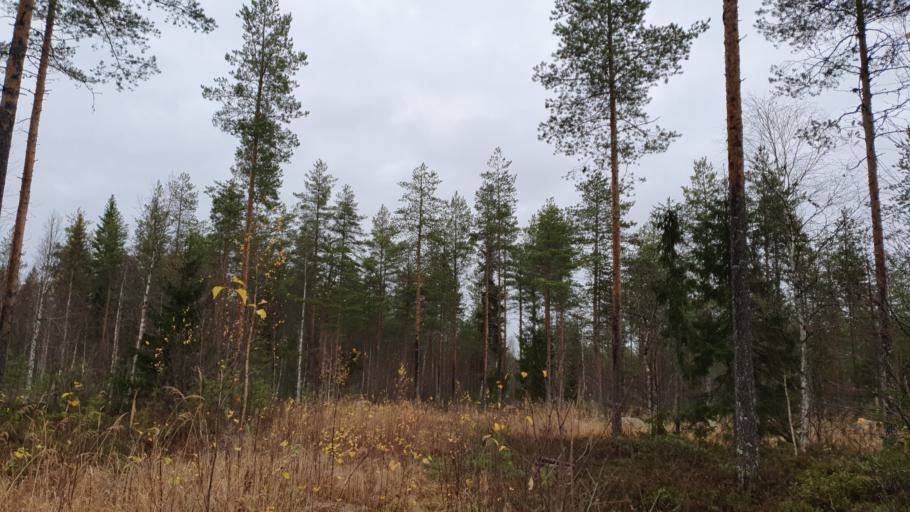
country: FI
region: Kainuu
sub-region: Kehys-Kainuu
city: Kuhmo
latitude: 64.1424
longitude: 29.4193
